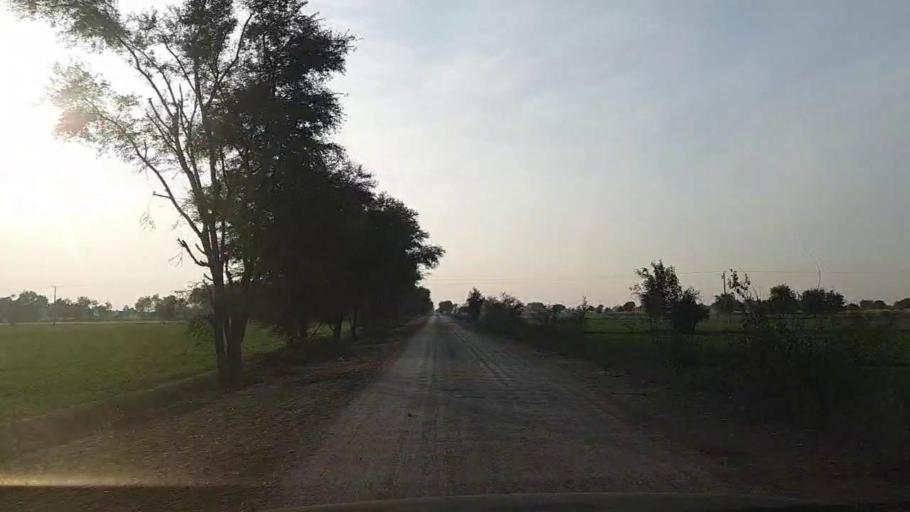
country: PK
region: Sindh
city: Jam Sahib
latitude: 26.4351
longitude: 68.5572
